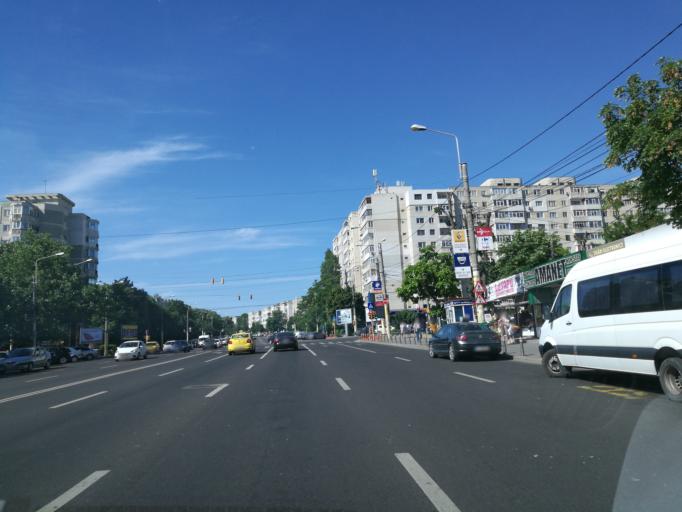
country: RO
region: Constanta
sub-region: Municipiul Constanta
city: Constanta
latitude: 44.2010
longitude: 28.6273
